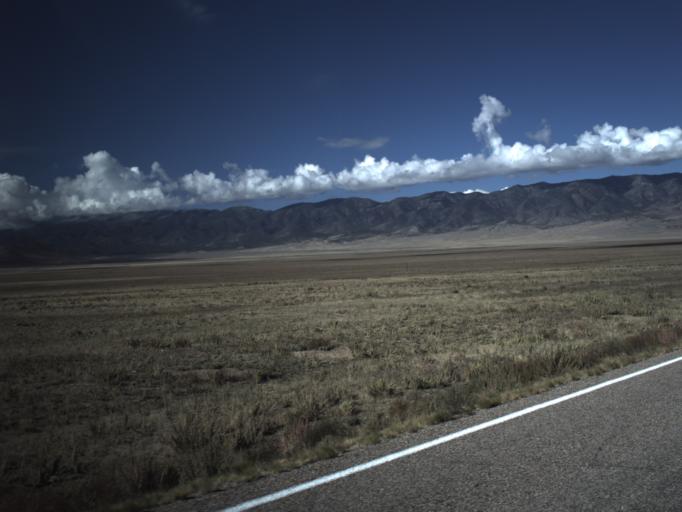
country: US
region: Utah
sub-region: Beaver County
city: Milford
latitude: 38.4559
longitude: -113.3620
